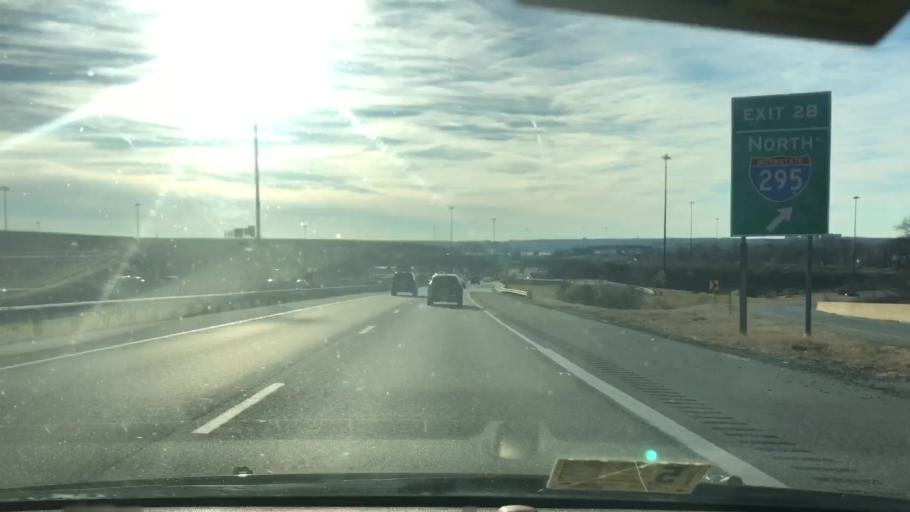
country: US
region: Maryland
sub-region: Prince George's County
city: Forest Heights
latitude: 38.7974
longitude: -77.0118
